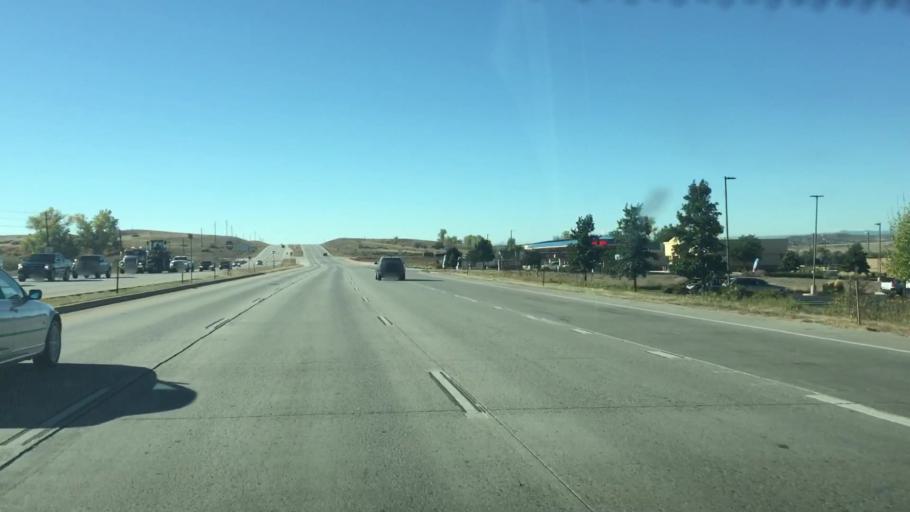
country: US
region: Colorado
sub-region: Douglas County
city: The Pinery
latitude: 39.4777
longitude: -104.7582
